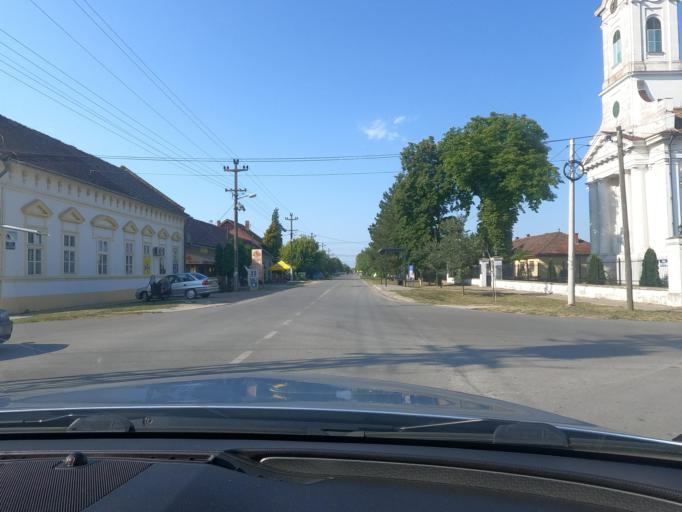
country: RS
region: Autonomna Pokrajina Vojvodina
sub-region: Juznobacki Okrug
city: Kovilj
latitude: 45.2213
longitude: 20.0200
